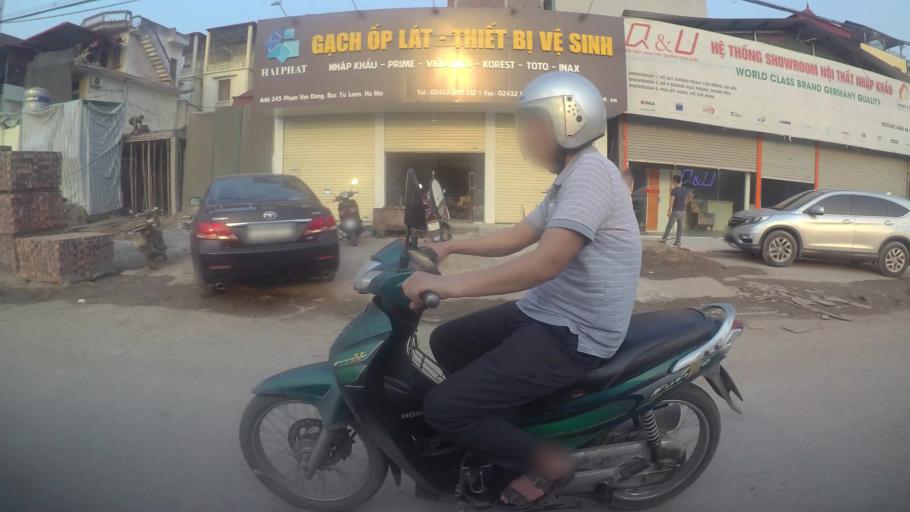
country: VN
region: Ha Noi
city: Tay Ho
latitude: 21.0734
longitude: 105.7858
